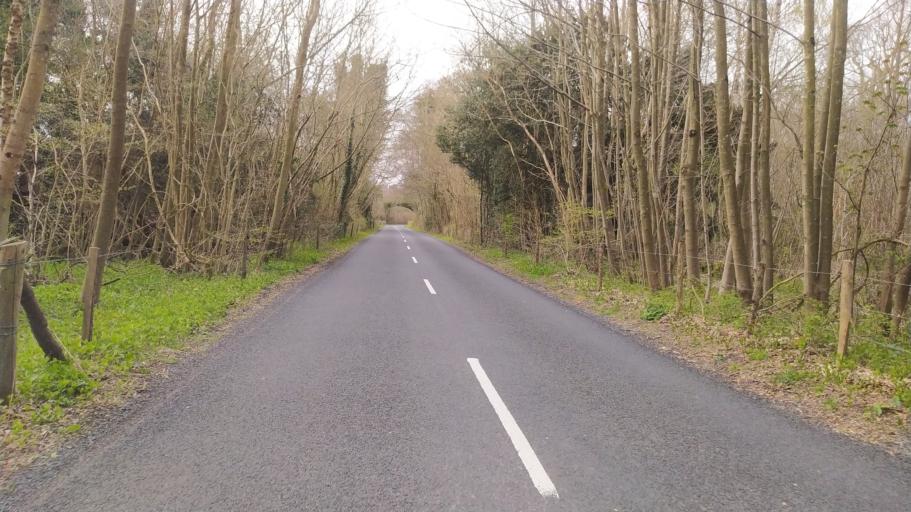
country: GB
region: England
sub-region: Hampshire
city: Bishops Waltham
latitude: 50.9996
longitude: -1.2016
